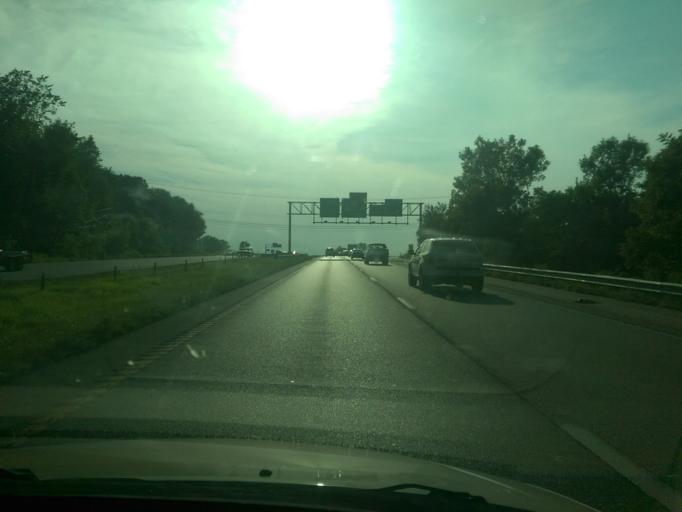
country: US
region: Missouri
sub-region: Clay County
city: Gladstone
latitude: 39.1793
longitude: -94.5706
